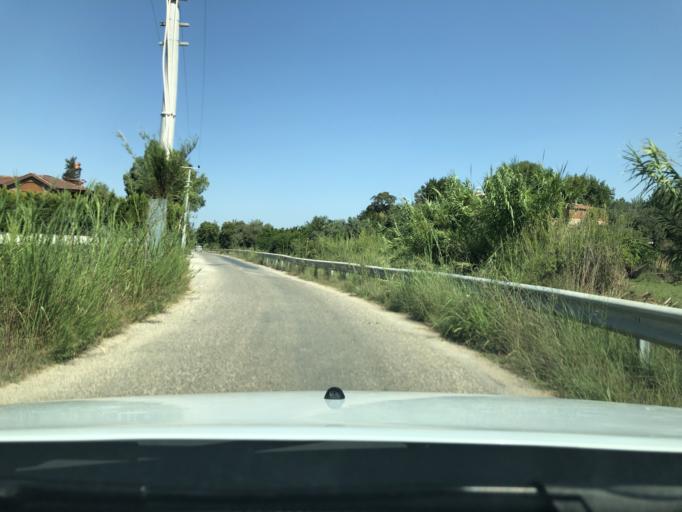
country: TR
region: Antalya
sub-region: Manavgat
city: Manavgat
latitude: 36.8025
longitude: 31.4690
